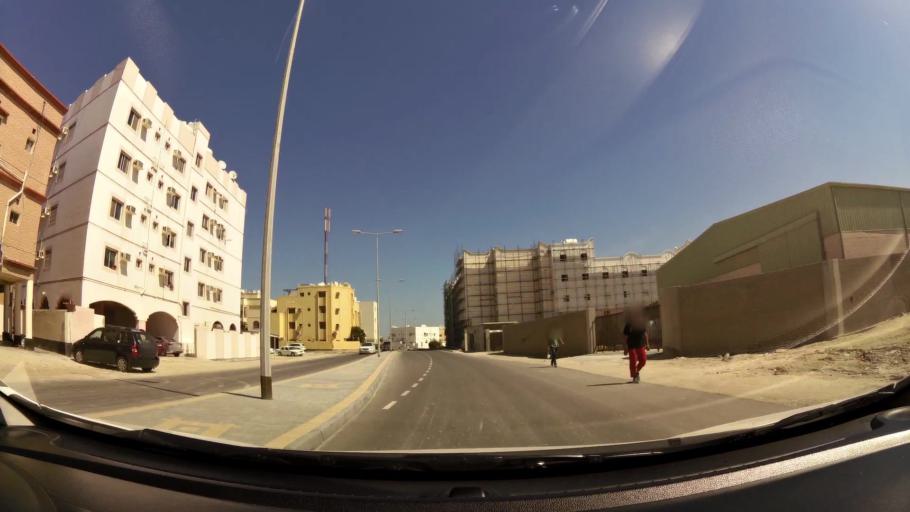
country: BH
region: Muharraq
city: Al Hadd
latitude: 26.2759
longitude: 50.6437
